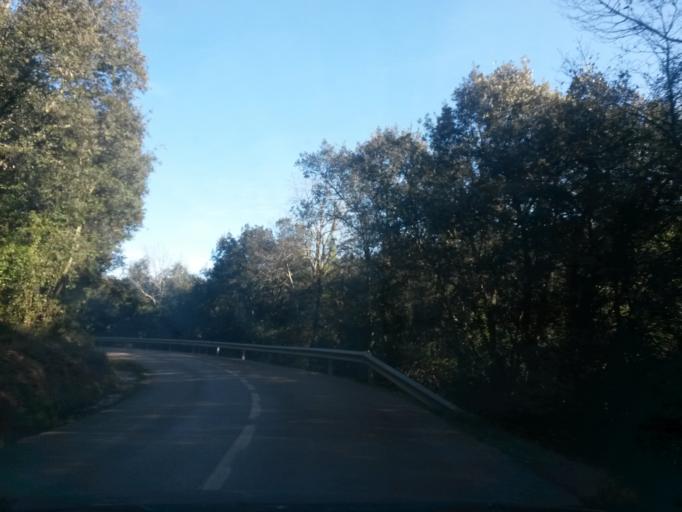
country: ES
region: Catalonia
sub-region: Provincia de Girona
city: la Cellera de Ter
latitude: 42.0131
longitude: 2.6738
